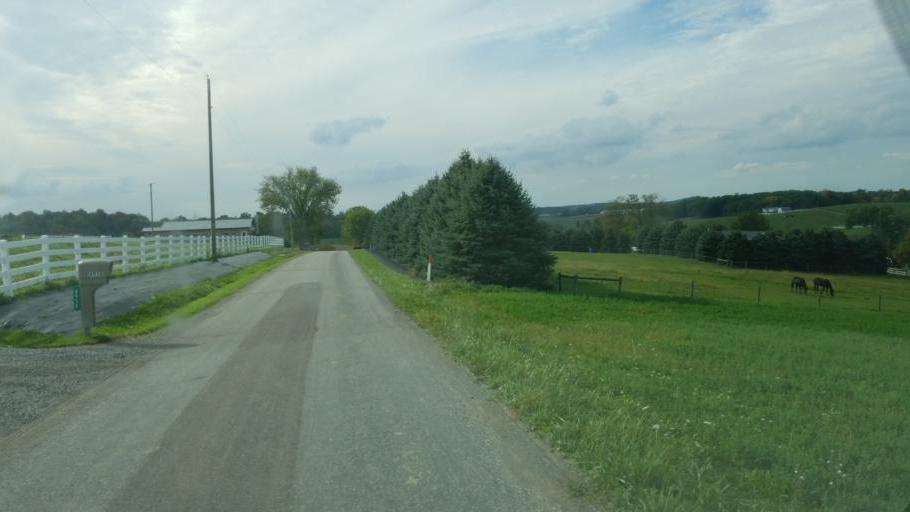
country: US
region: Ohio
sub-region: Holmes County
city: Millersburg
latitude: 40.6074
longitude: -81.7972
